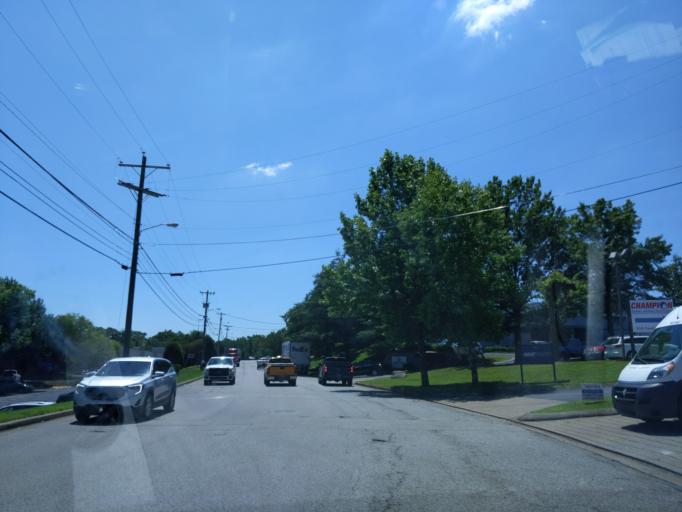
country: US
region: Tennessee
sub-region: Davidson County
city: Nashville
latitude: 36.1478
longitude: -86.7419
